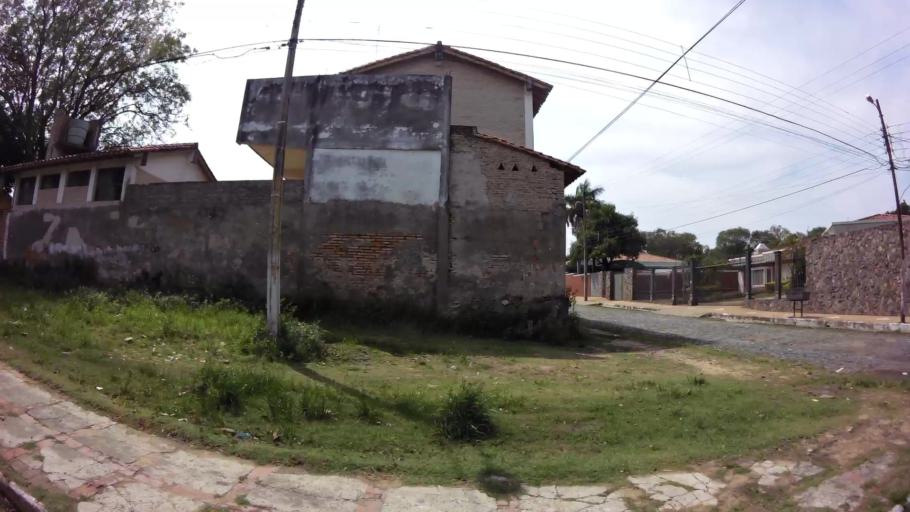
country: PY
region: Asuncion
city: Asuncion
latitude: -25.2645
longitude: -57.5857
